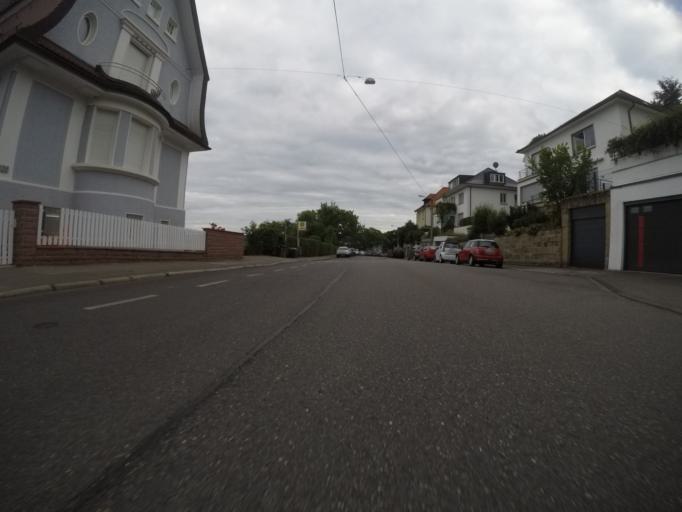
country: DE
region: Baden-Wuerttemberg
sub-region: Regierungsbezirk Stuttgart
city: Stuttgart Feuerbach
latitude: 48.7823
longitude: 9.1491
